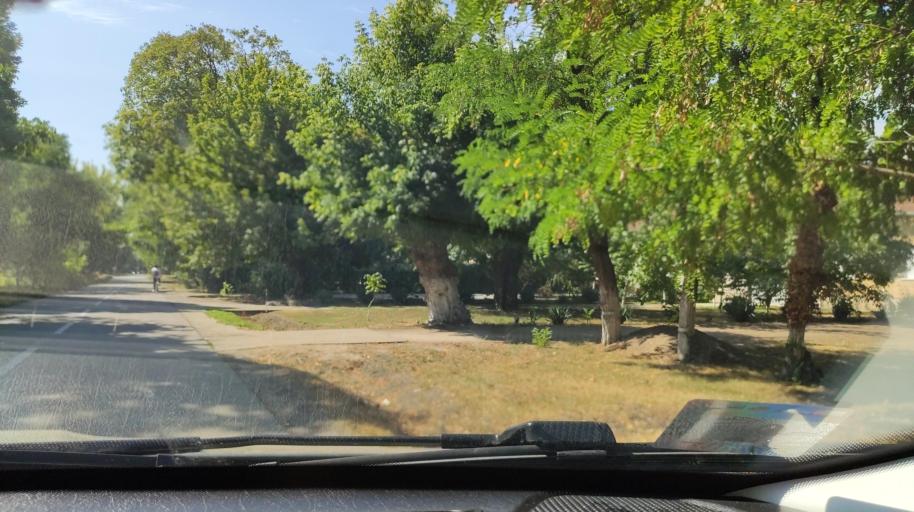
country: RS
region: Autonomna Pokrajina Vojvodina
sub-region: Severnobacki Okrug
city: Backa Topola
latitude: 45.8204
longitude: 19.6441
